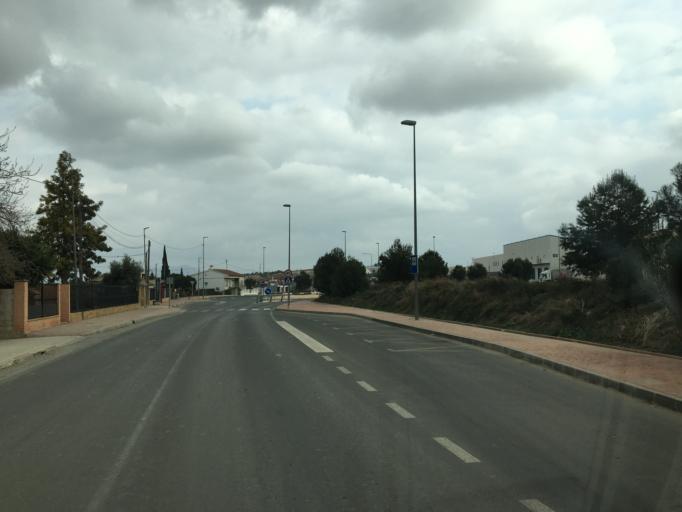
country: ES
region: Murcia
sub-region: Murcia
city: Beniel
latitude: 38.0191
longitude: -0.9844
